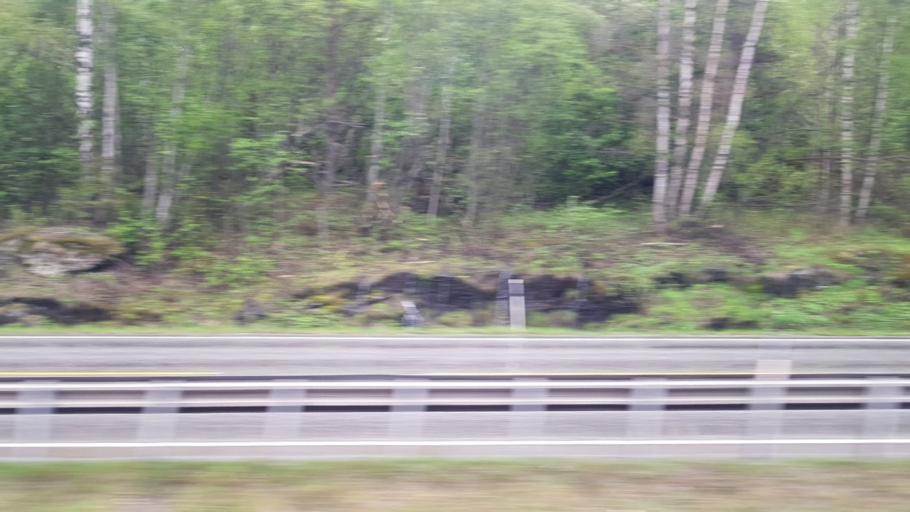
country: NO
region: Oppland
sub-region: Nord-Fron
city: Vinstra
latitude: 61.6193
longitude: 9.7139
